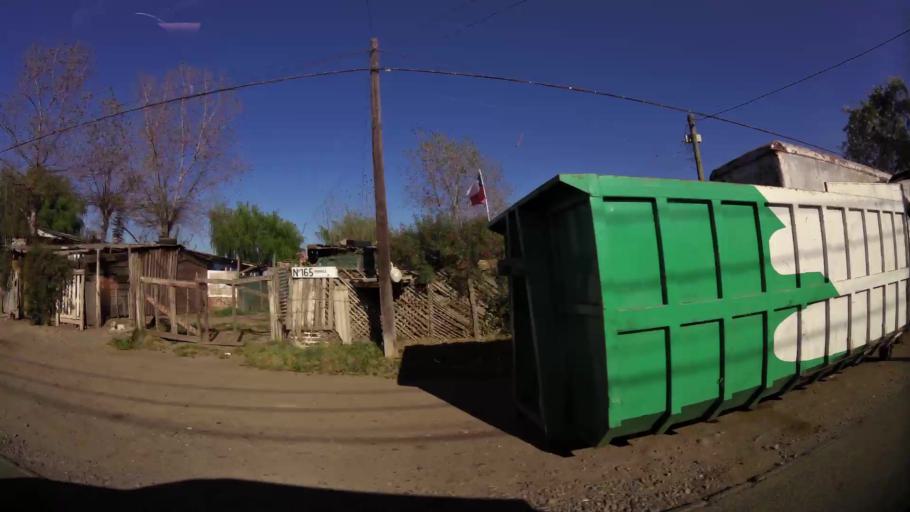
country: CL
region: Santiago Metropolitan
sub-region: Provincia de Talagante
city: Penaflor
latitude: -33.6086
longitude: -70.8597
